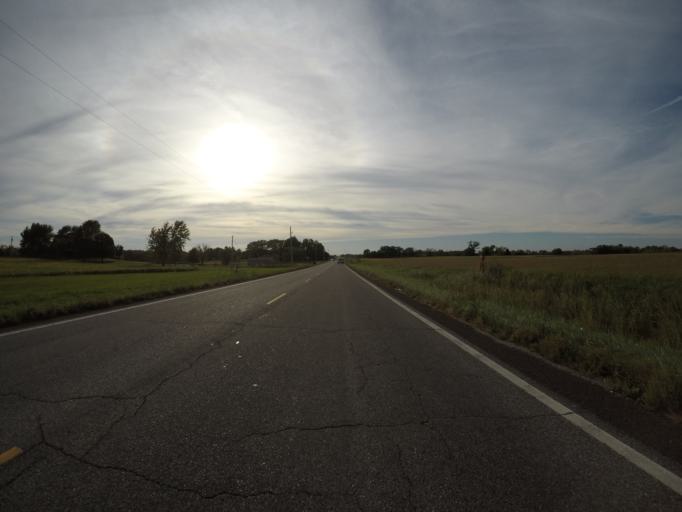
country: US
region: Kansas
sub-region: Douglas County
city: Baldwin City
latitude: 38.7823
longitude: -95.2113
